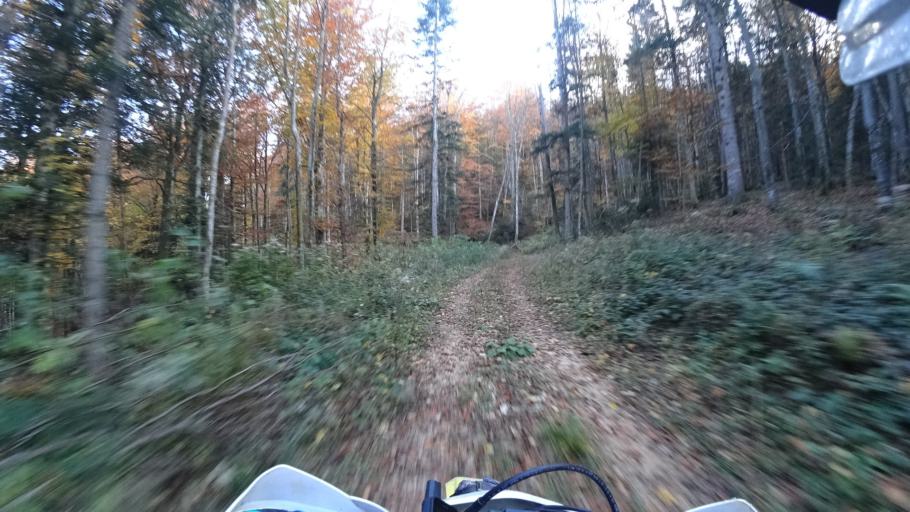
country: HR
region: Karlovacka
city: Plaski
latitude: 44.9645
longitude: 15.3950
